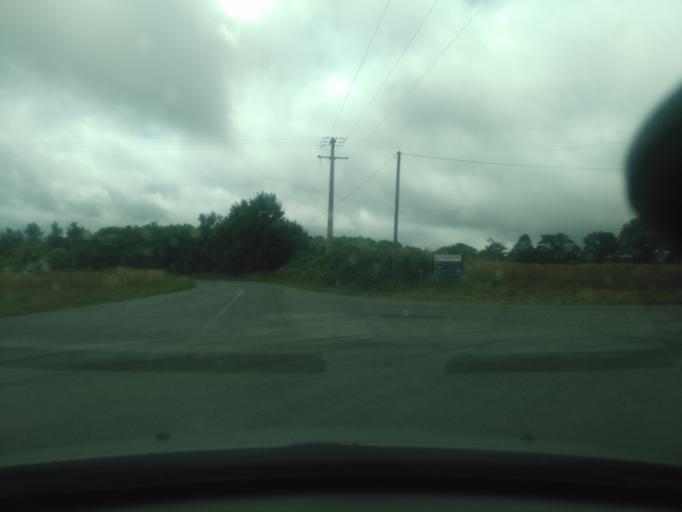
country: FR
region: Brittany
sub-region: Departement des Cotes-d'Armor
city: Quintin
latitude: 48.3188
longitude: -2.9559
